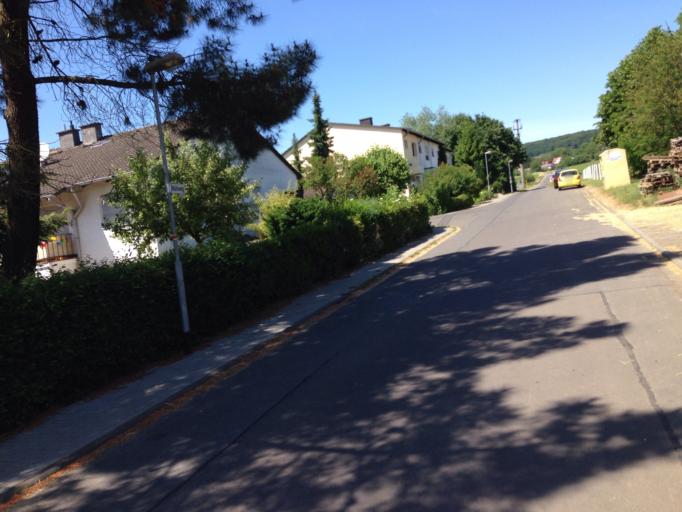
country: DE
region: Hesse
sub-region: Regierungsbezirk Giessen
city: Alten Buseck
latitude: 50.6116
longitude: 8.7616
